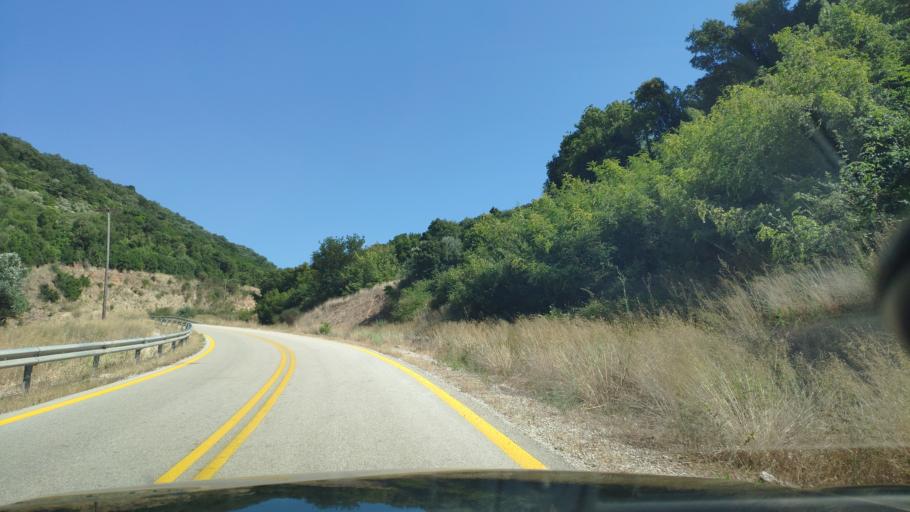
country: GR
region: West Greece
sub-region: Nomos Aitolias kai Akarnanias
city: Amfilochia
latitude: 38.8600
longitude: 21.0834
